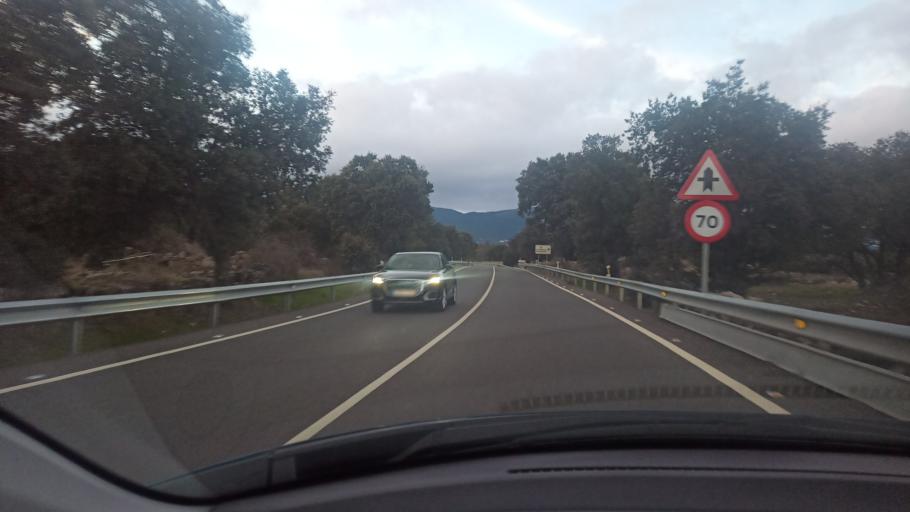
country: ES
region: Madrid
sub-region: Provincia de Madrid
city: El Escorial
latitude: 40.5402
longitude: -4.1023
